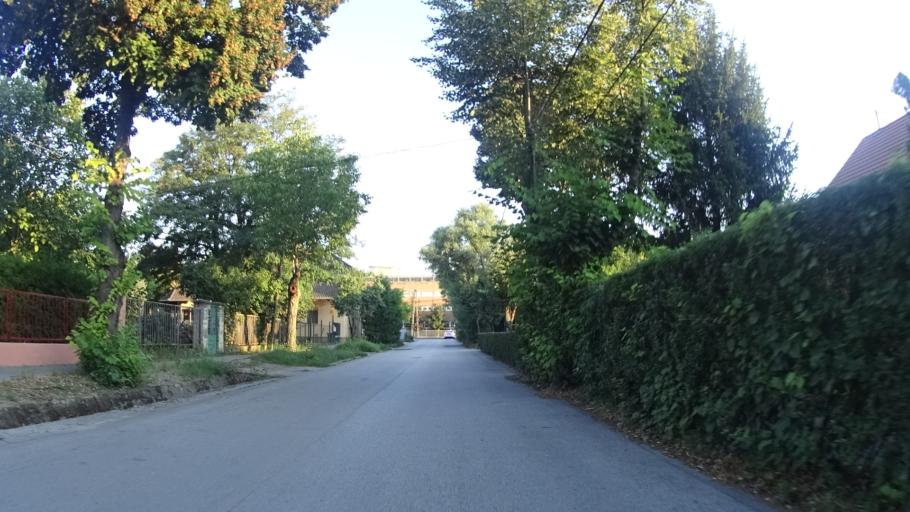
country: HU
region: Pest
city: Halasztelek
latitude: 47.3976
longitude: 19.0024
